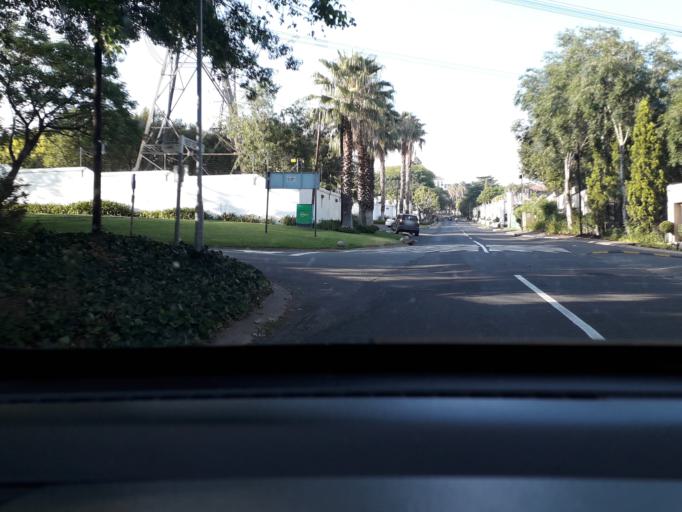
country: ZA
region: Gauteng
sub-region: City of Johannesburg Metropolitan Municipality
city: Modderfontein
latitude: -26.0851
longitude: 28.0567
